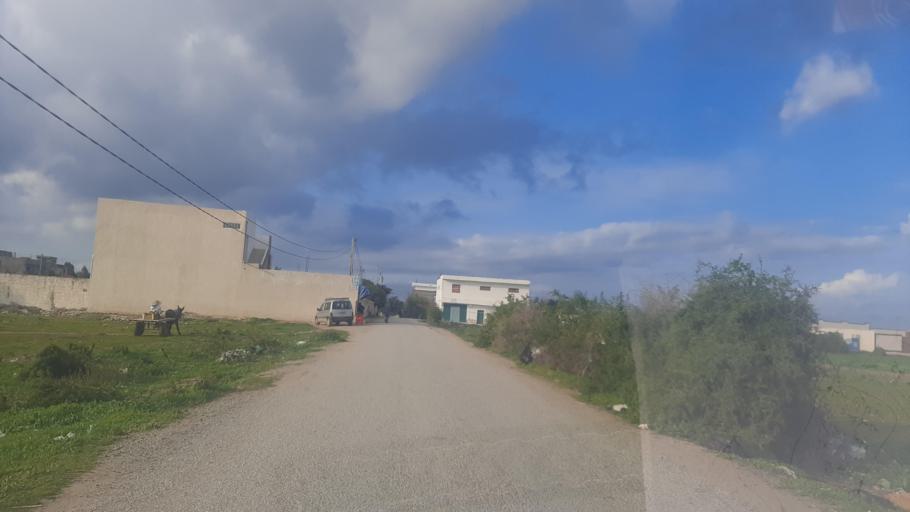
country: TN
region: Nabul
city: Manzil Bu Zalafah
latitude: 36.7155
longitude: 10.4972
